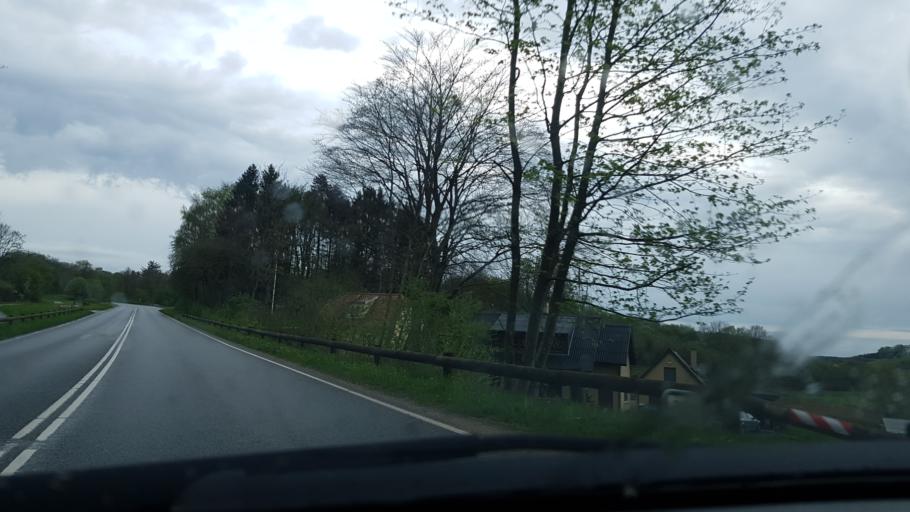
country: DK
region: South Denmark
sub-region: Kolding Kommune
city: Kolding
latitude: 55.4815
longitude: 9.4174
